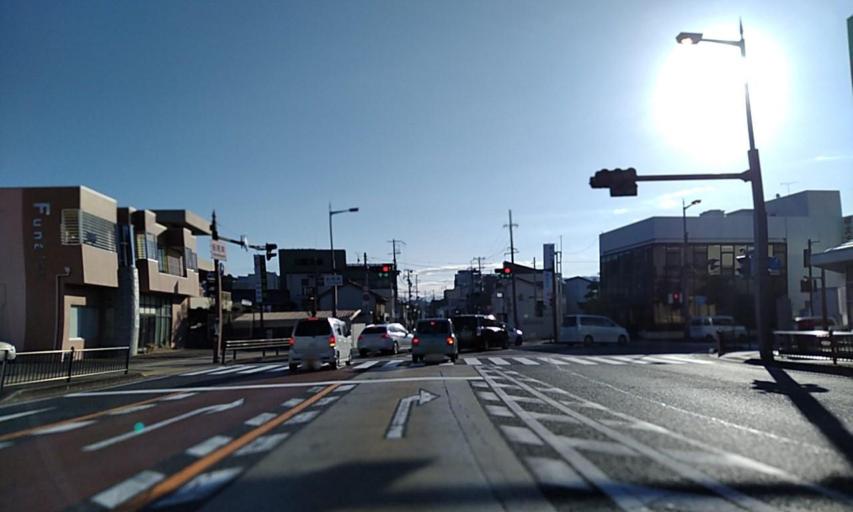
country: JP
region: Wakayama
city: Kainan
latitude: 34.1588
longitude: 135.2051
